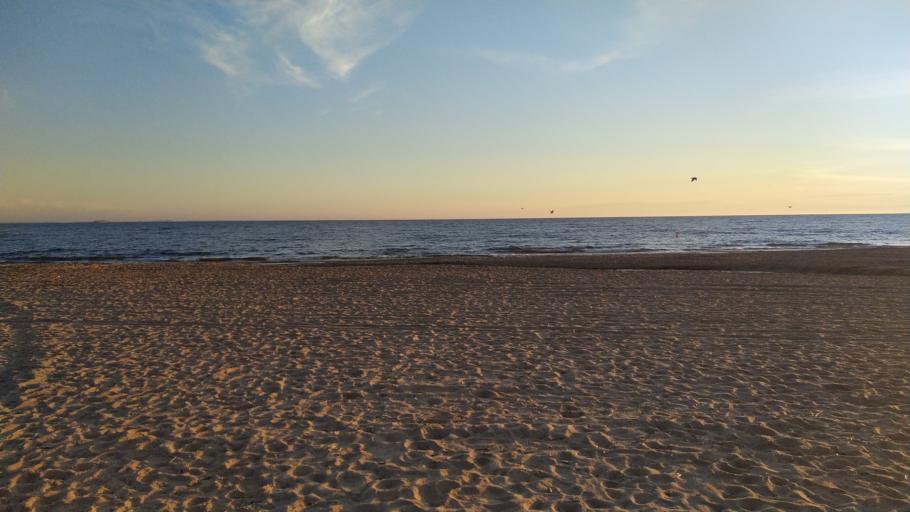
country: RU
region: St.-Petersburg
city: Solnechnoye
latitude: 60.1454
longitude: 29.9258
